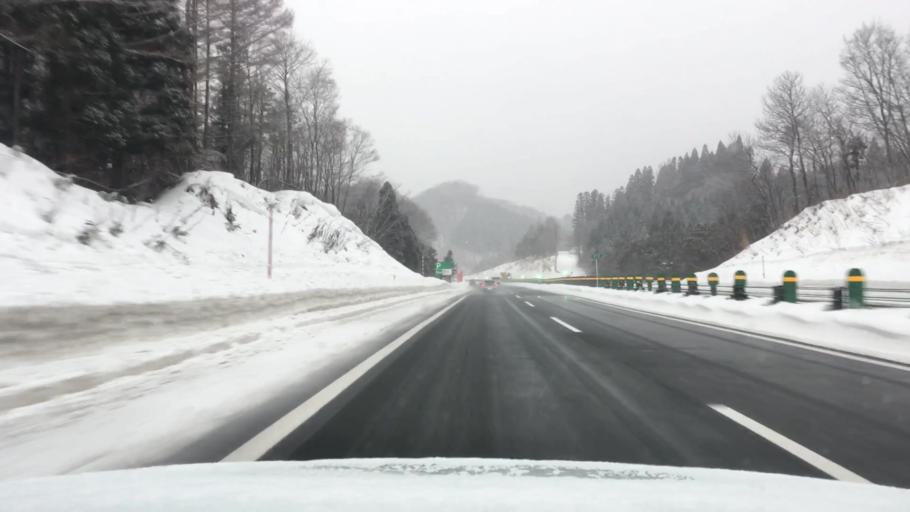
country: JP
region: Akita
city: Hanawa
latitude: 40.1347
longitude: 140.9749
